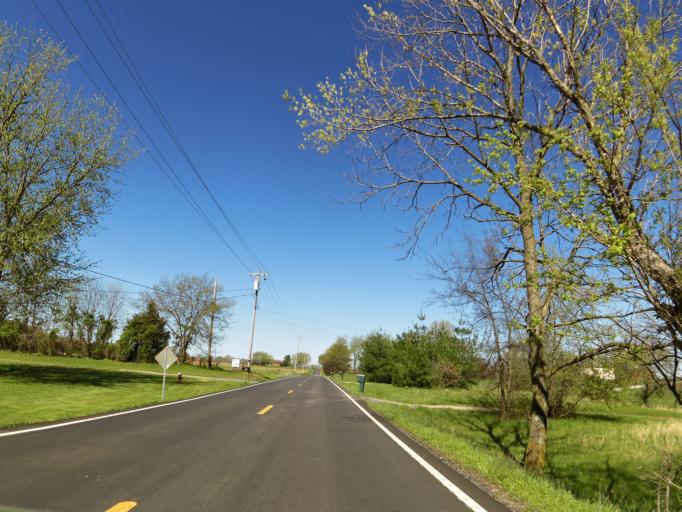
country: US
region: Tennessee
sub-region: Robertson County
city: Springfield
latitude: 36.5649
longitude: -86.8474
